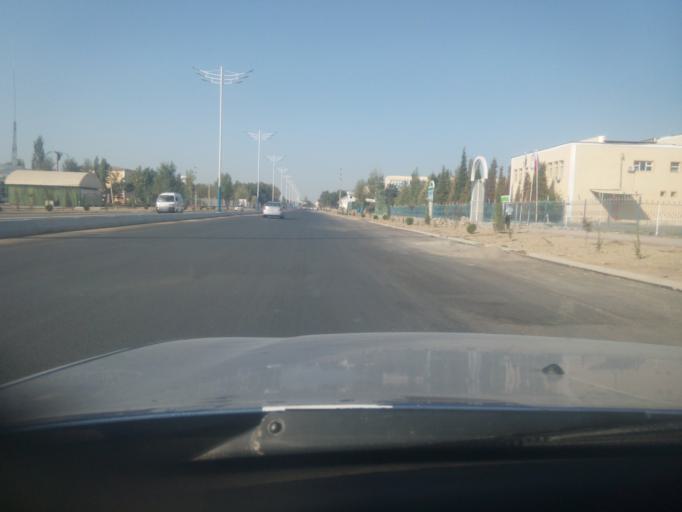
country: UZ
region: Sirdaryo
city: Guliston
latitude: 40.5150
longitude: 68.7867
